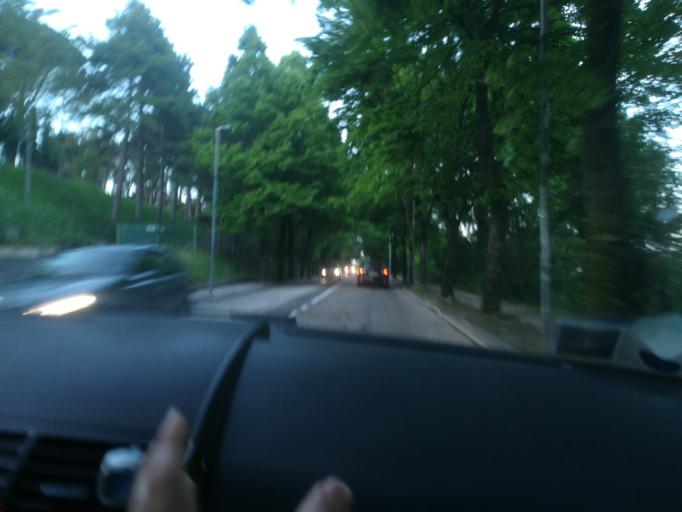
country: IT
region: The Marches
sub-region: Provincia di Macerata
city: Villa Potenza
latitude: 43.2964
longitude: 13.4262
